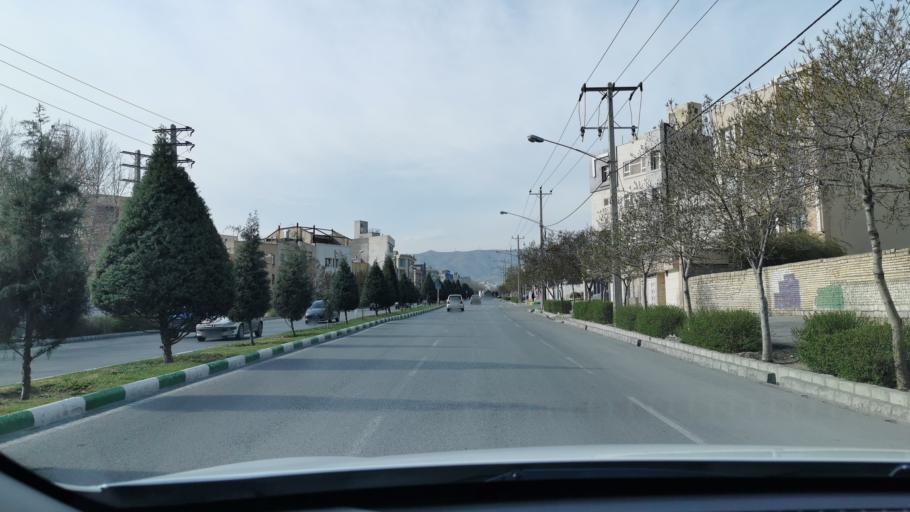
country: IR
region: Razavi Khorasan
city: Mashhad
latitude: 36.3078
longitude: 59.5143
